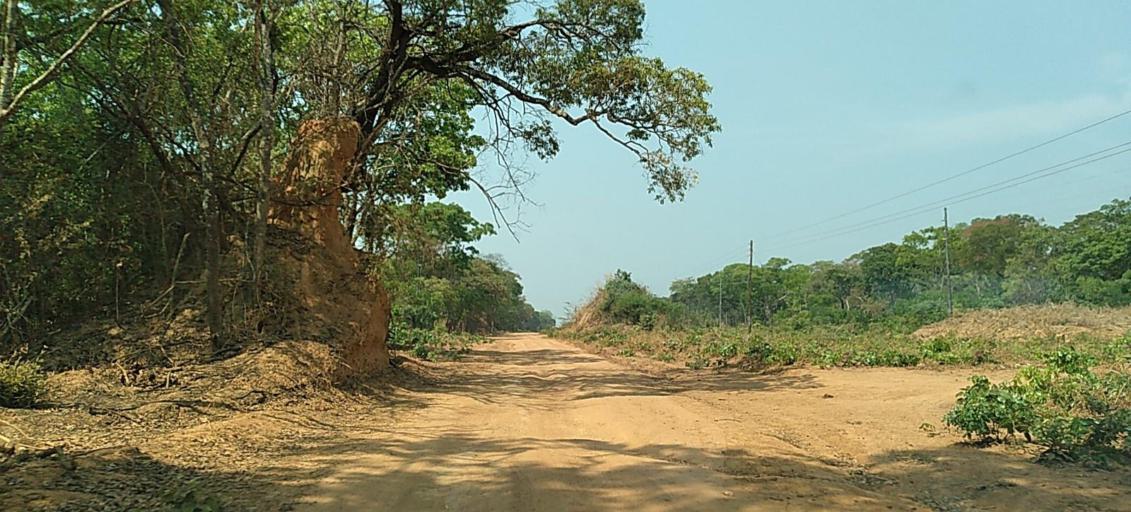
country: ZM
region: Copperbelt
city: Chingola
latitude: -13.0513
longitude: 27.4288
